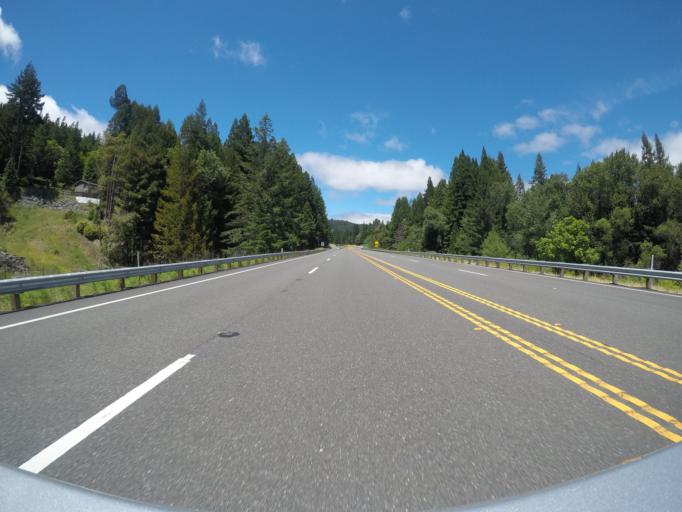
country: US
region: California
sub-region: Humboldt County
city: Redway
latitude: 40.2463
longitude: -123.8316
